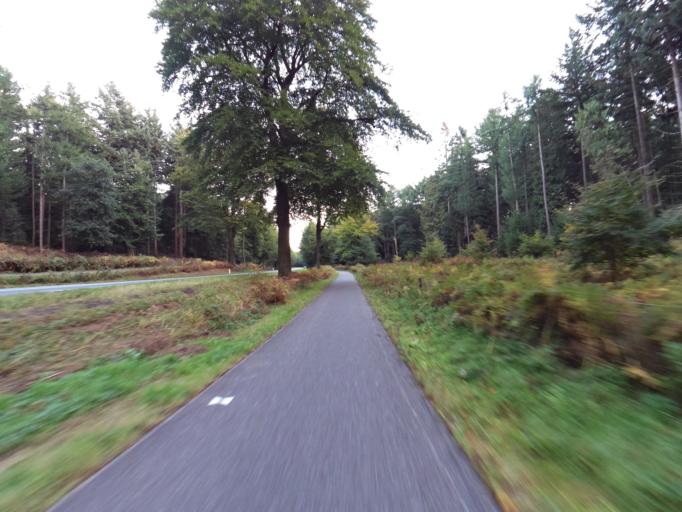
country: NL
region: Gelderland
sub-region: Gemeente Montferland
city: s-Heerenberg
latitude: 51.9066
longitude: 6.2284
